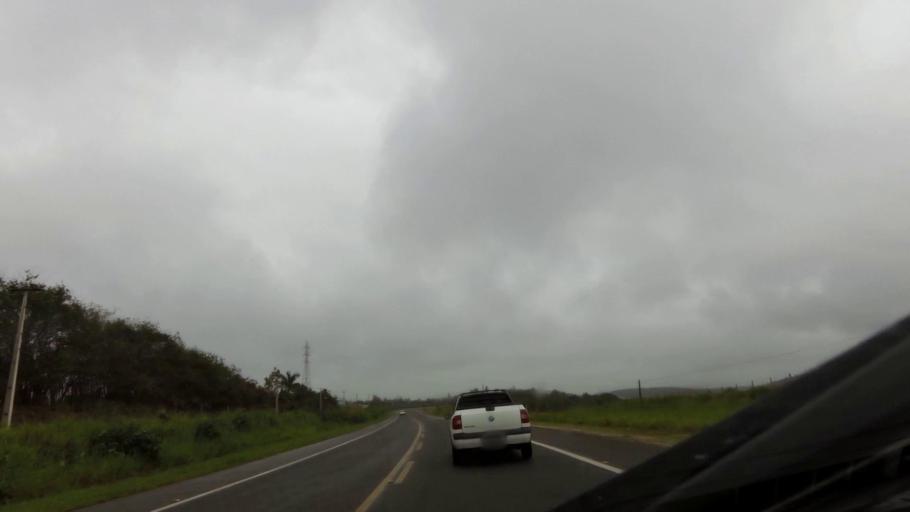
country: BR
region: Espirito Santo
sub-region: Guarapari
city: Guarapari
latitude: -20.7262
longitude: -40.5636
